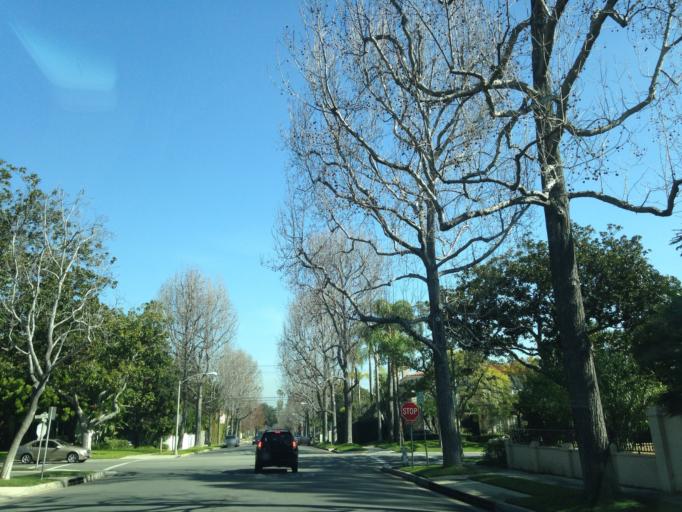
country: US
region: California
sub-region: Los Angeles County
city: Beverly Hills
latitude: 34.0757
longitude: -118.4046
